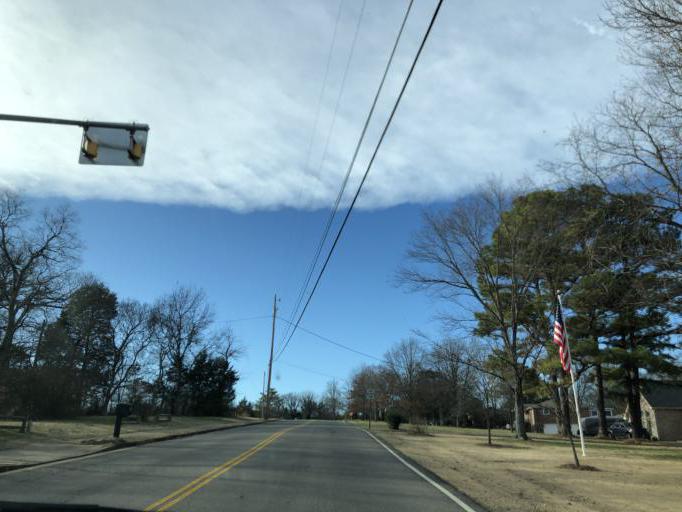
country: US
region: Tennessee
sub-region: Wilson County
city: Green Hill
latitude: 36.1578
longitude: -86.5802
